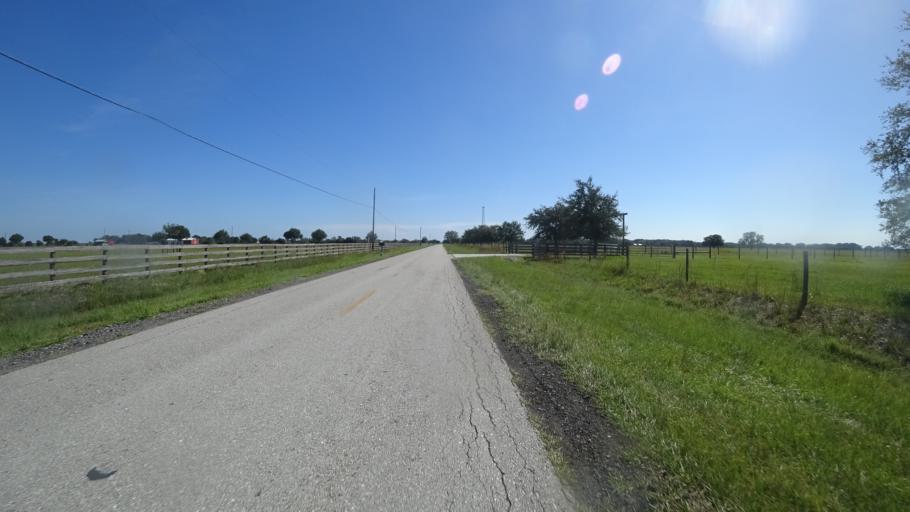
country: US
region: Florida
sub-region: Sarasota County
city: Warm Mineral Springs
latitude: 27.2739
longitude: -82.1899
